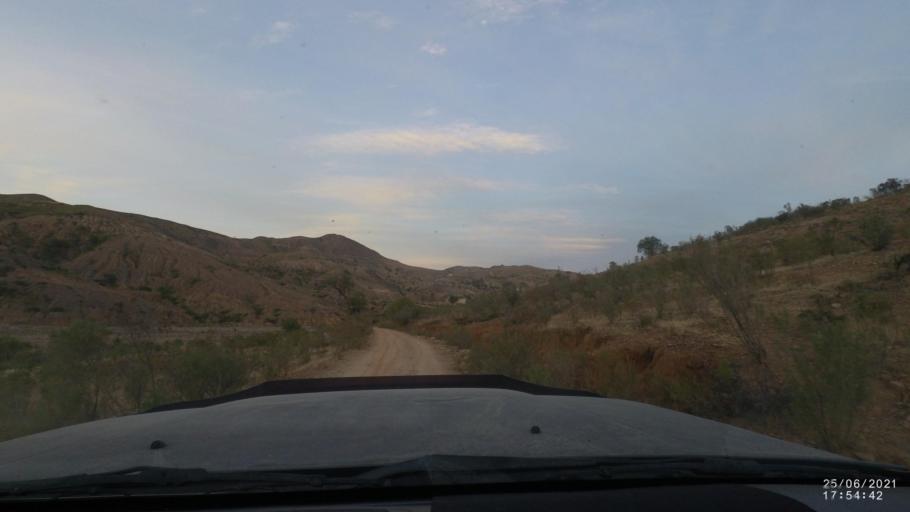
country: BO
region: Cochabamba
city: Mizque
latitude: -17.9420
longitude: -65.6367
